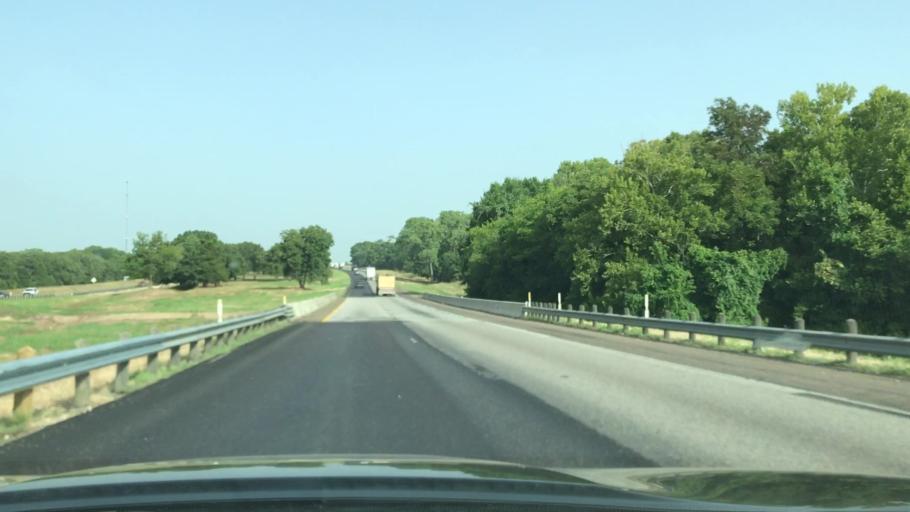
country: US
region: Texas
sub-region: Van Zandt County
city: Wills Point
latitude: 32.6612
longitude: -96.1155
